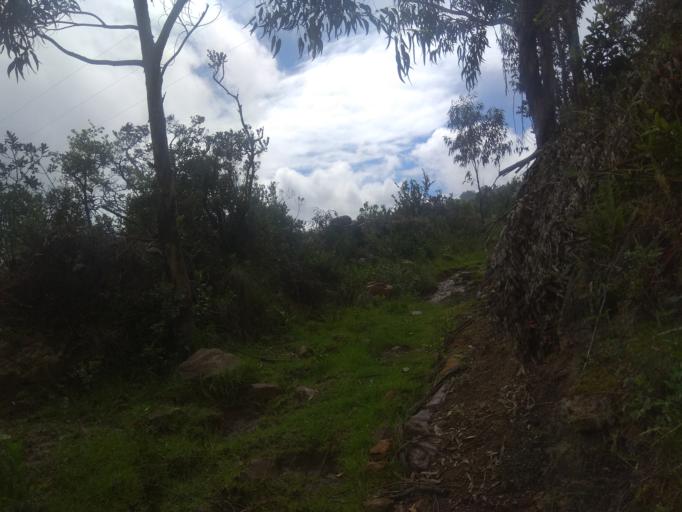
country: CO
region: Boyaca
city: Socota
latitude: 6.0097
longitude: -72.6739
